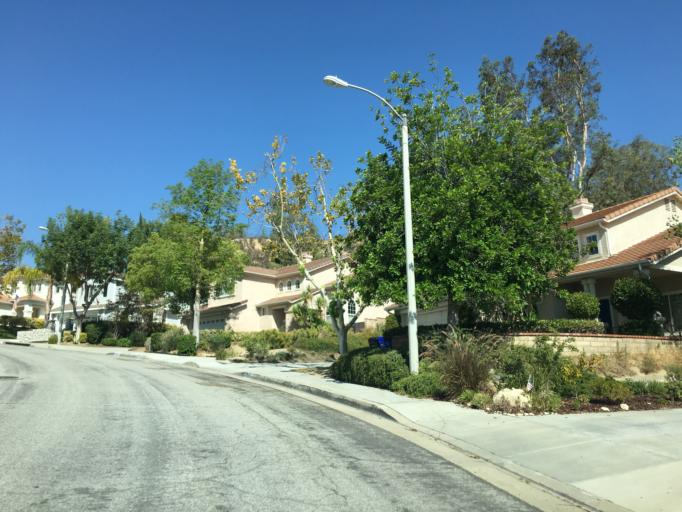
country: US
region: California
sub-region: Los Angeles County
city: Castaic
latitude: 34.4739
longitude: -118.6211
